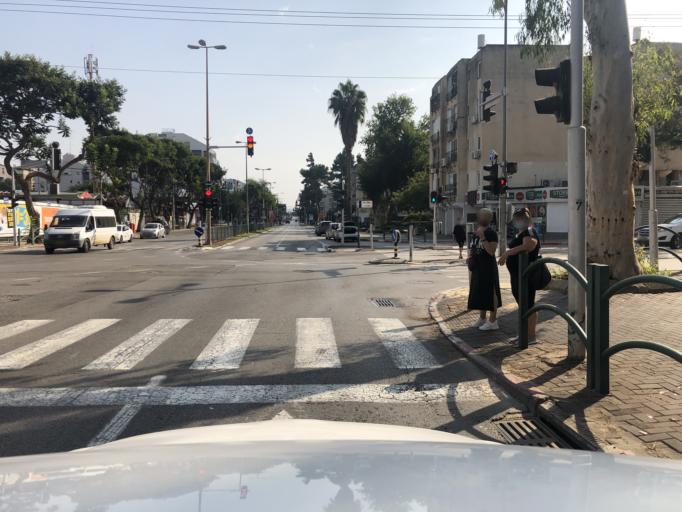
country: IL
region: Central District
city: Kfar Saba
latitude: 32.1740
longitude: 34.9138
